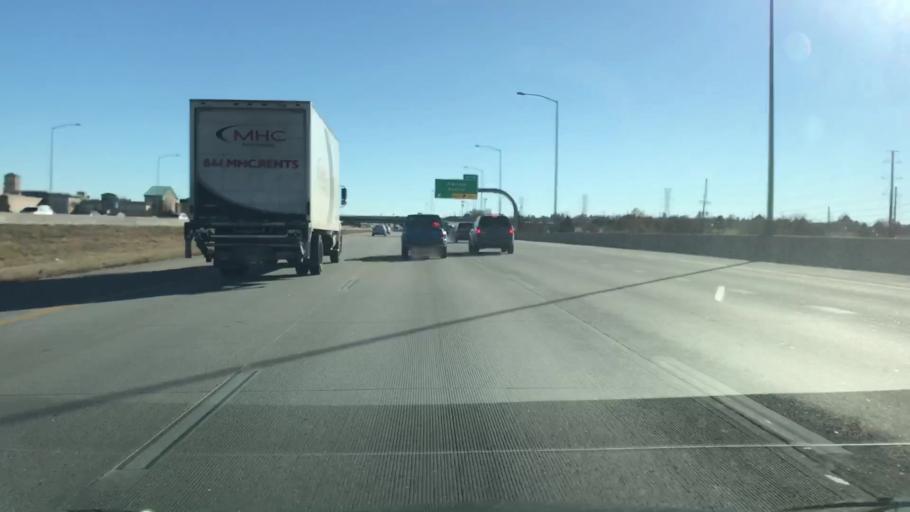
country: US
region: Colorado
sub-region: Adams County
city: Aurora
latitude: 39.7178
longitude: -104.8270
